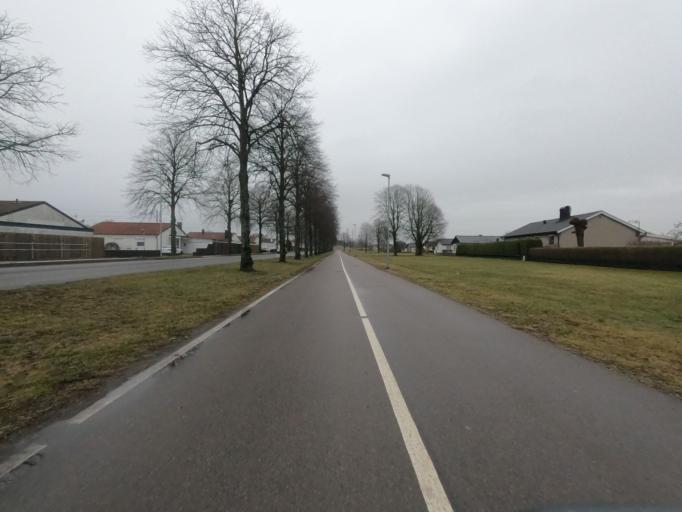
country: SE
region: Halland
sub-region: Halmstads Kommun
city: Fyllinge
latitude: 56.6719
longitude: 12.8938
